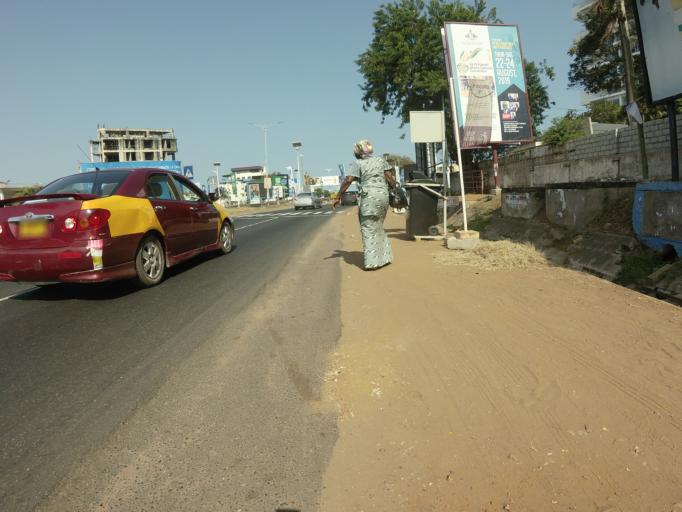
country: GH
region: Greater Accra
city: Accra
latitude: 5.5672
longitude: -0.1816
